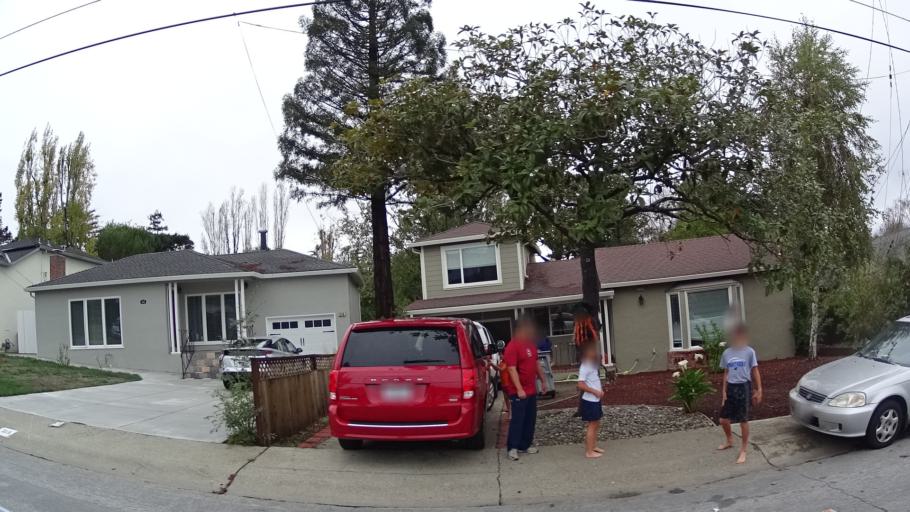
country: US
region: California
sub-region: San Mateo County
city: San Bruno
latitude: 37.6115
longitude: -122.4096
